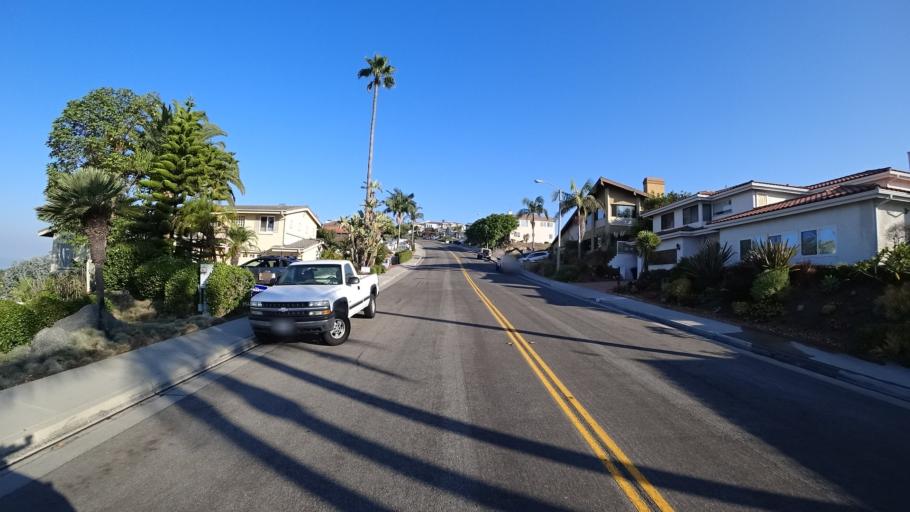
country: US
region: California
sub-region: Orange County
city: San Clemente
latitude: 33.4199
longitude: -117.5982
